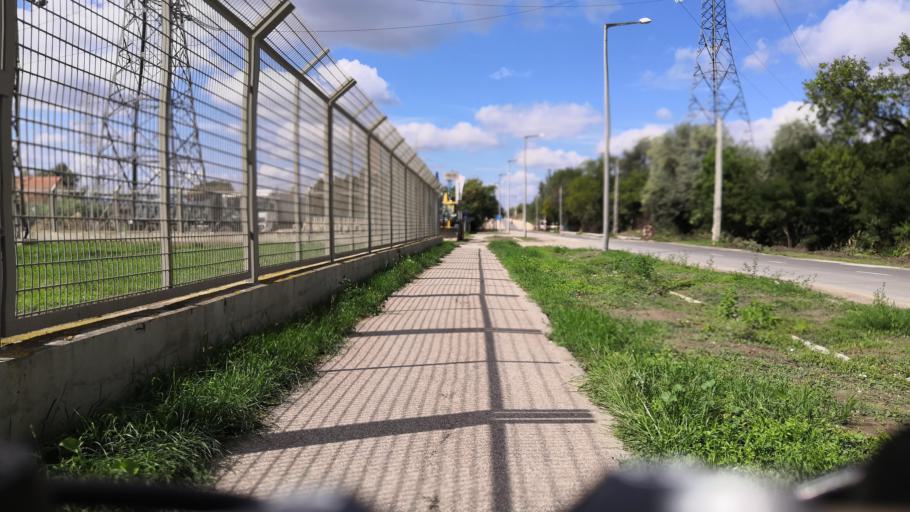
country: HU
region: Csongrad
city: Szeged
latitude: 46.2756
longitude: 20.1394
